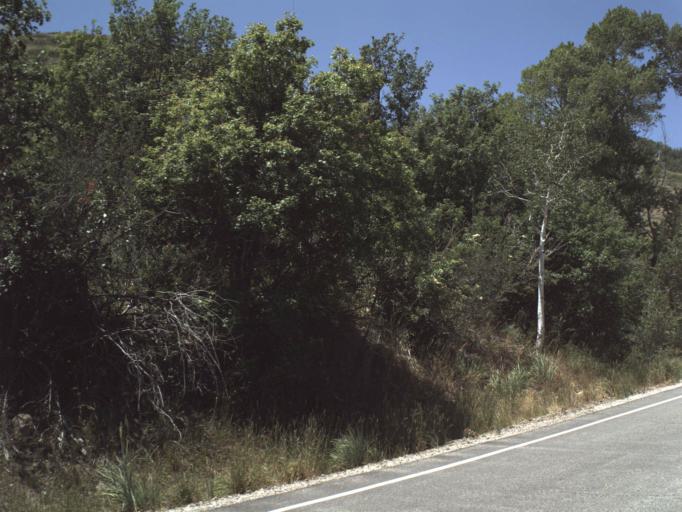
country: US
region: Utah
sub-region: Weber County
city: Wolf Creek
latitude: 41.3497
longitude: -111.5958
